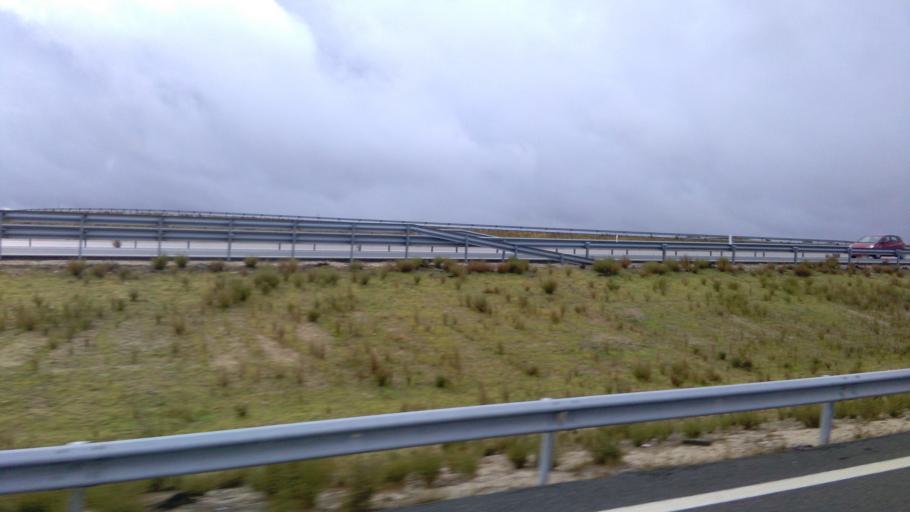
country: ES
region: Castille-La Mancha
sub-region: Province of Toledo
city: Las Ventas de Retamosa
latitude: 40.1878
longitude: -4.1222
